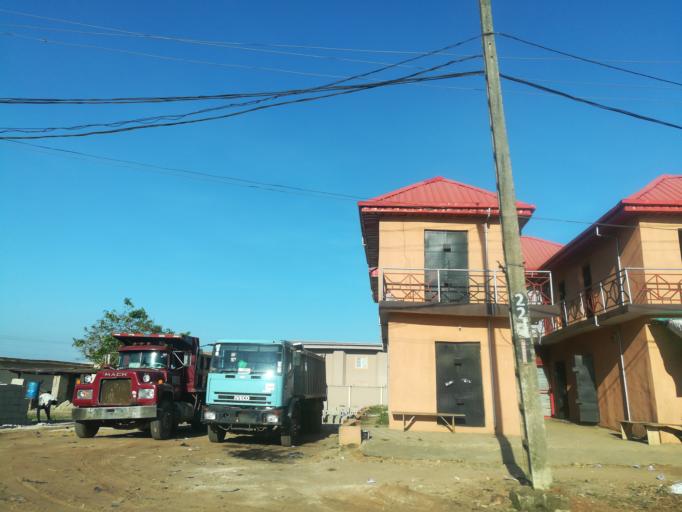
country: NG
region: Lagos
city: Ikorodu
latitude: 6.5651
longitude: 3.5348
